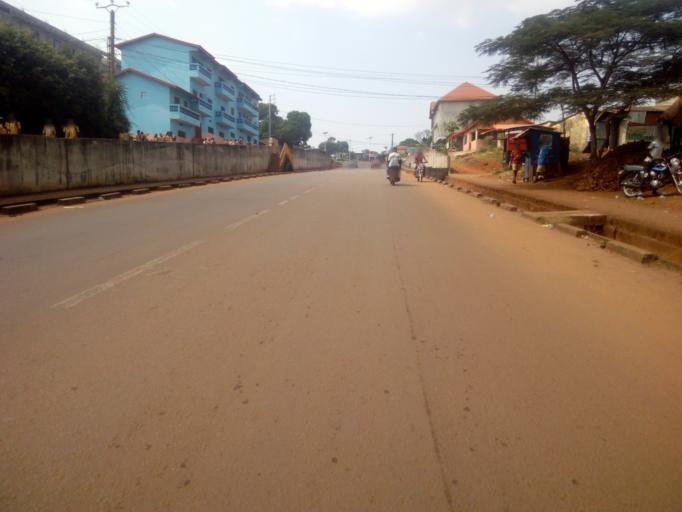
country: GN
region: Conakry
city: Conakry
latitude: 9.6361
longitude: -13.5741
